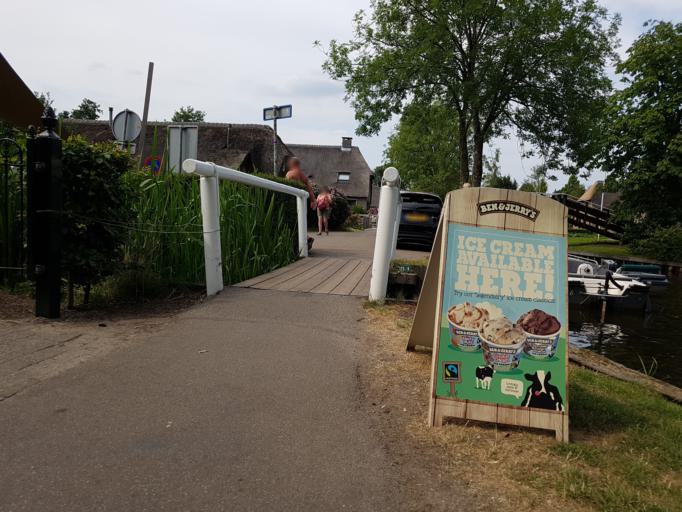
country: NL
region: Overijssel
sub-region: Gemeente Steenwijkerland
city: Giethoorn
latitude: 52.7269
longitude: 6.0901
